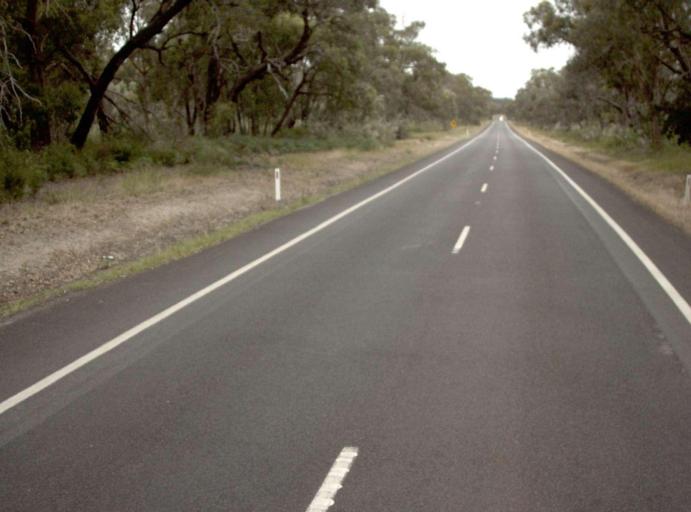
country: AU
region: Victoria
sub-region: Wellington
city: Sale
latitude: -38.3168
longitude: 147.0249
